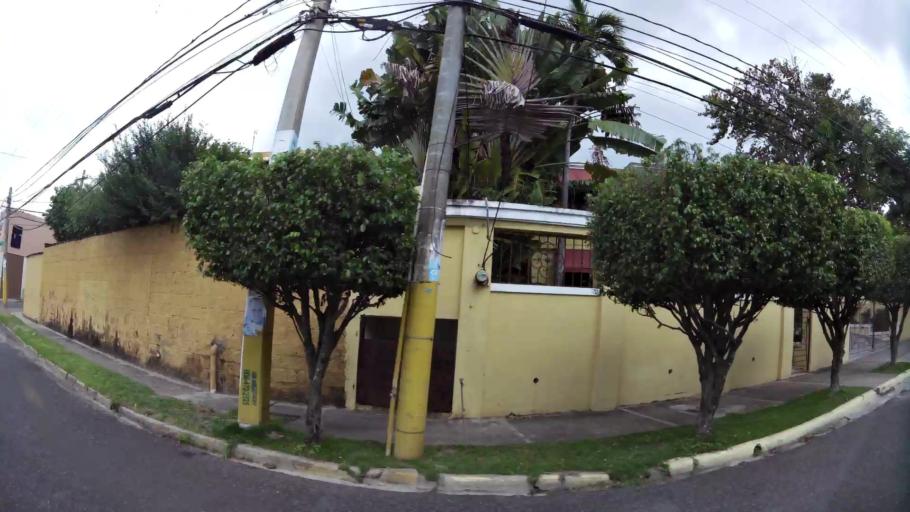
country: DO
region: Nacional
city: La Agustina
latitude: 18.4963
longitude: -69.9346
